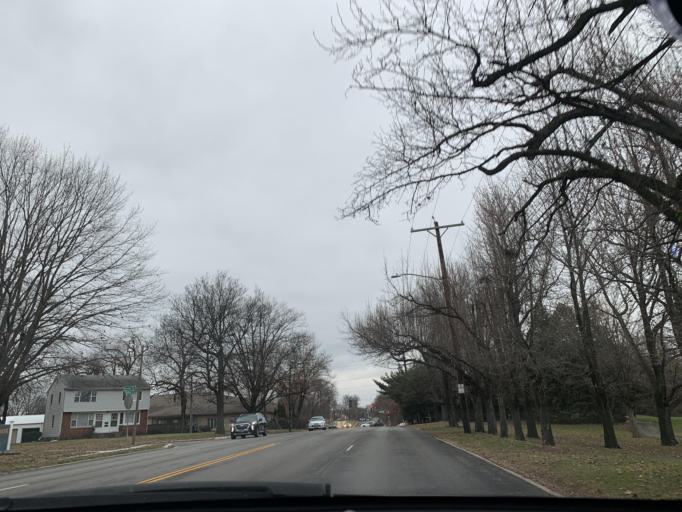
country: US
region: Illinois
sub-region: Sangamon County
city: Leland Grove
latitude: 39.7924
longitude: -89.6869
